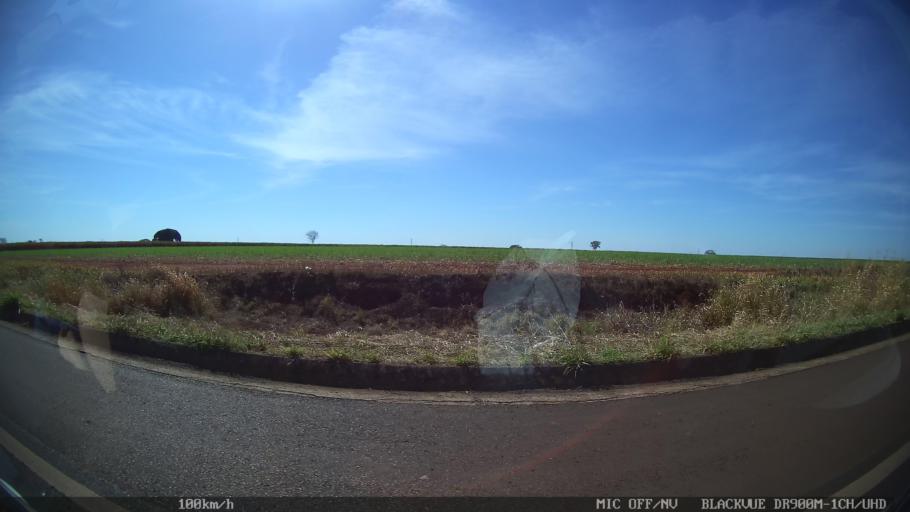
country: BR
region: Sao Paulo
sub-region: Ipua
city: Ipua
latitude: -20.4777
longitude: -48.0872
